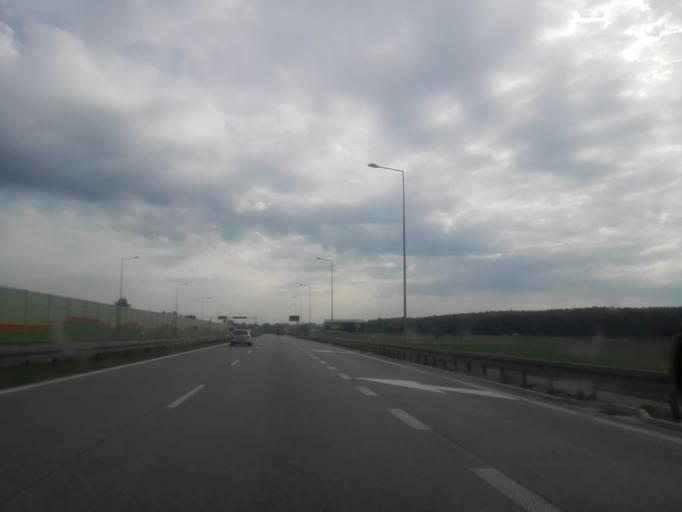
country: PL
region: Lodz Voivodeship
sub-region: Powiat tomaszowski
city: Lubochnia
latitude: 51.5919
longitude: 20.0465
